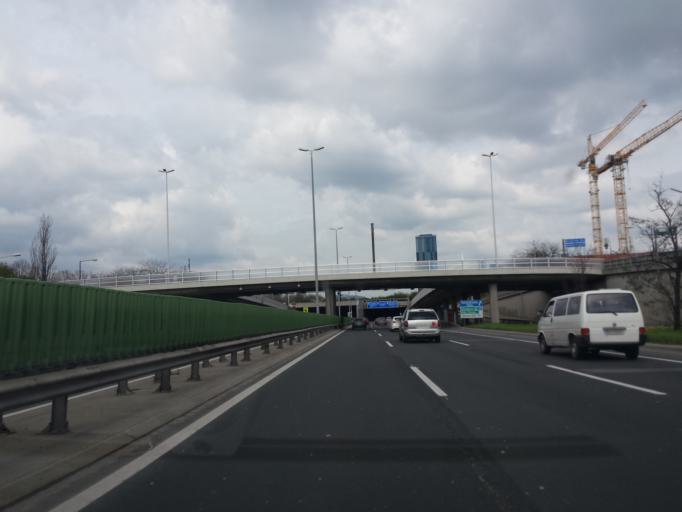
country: AT
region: Vienna
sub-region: Wien Stadt
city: Vienna
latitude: 48.2194
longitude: 16.4287
